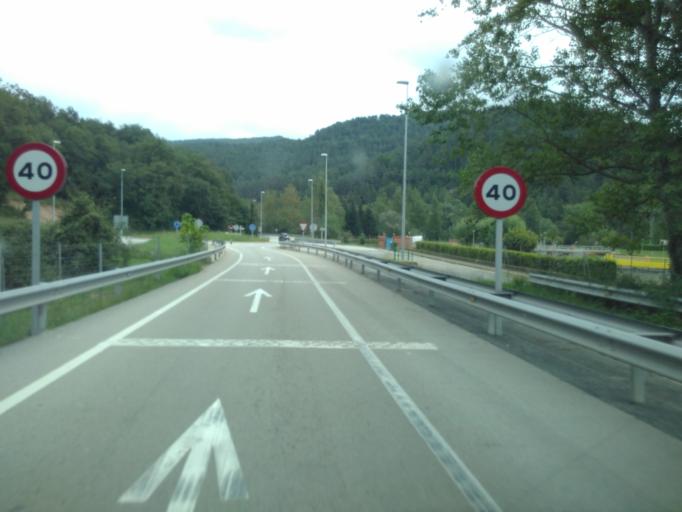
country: ES
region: Catalonia
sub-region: Provincia de Girona
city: Ripoll
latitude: 42.1647
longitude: 2.1983
